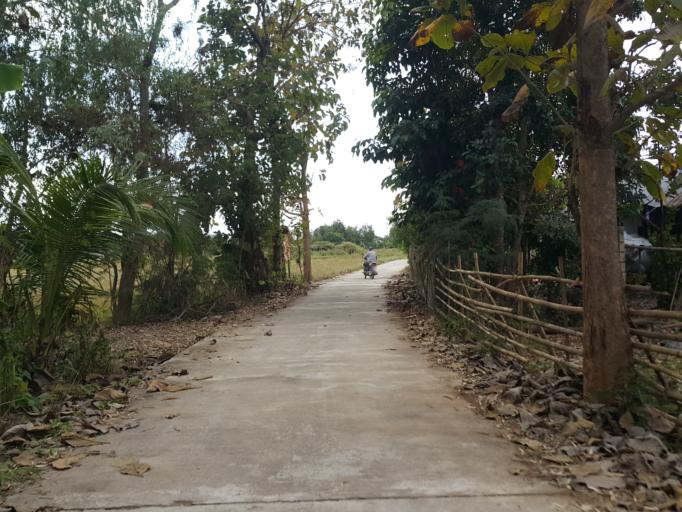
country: TH
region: Chiang Mai
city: San Kamphaeng
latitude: 18.8397
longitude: 99.1532
